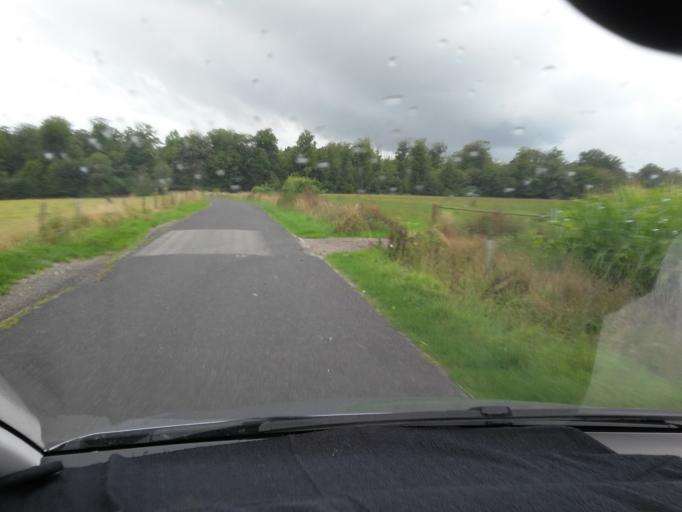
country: BE
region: Wallonia
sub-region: Province du Luxembourg
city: Attert
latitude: 49.7423
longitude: 5.8086
